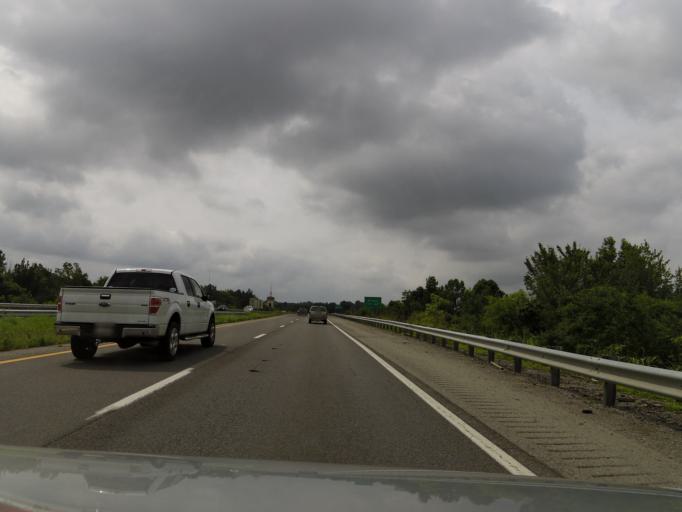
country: US
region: Kentucky
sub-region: Hopkins County
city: Madisonville
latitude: 37.3409
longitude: -87.4800
